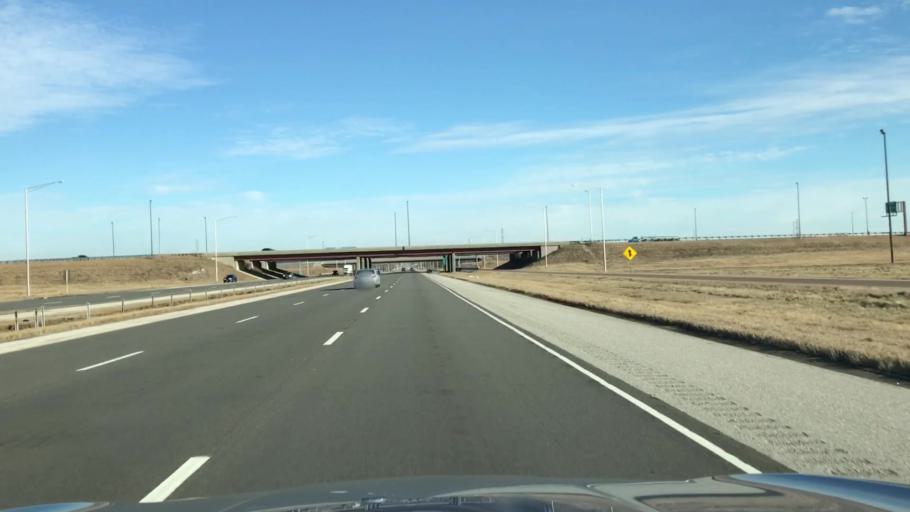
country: US
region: Illinois
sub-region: Madison County
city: Mitchell
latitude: 38.7571
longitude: -90.0469
